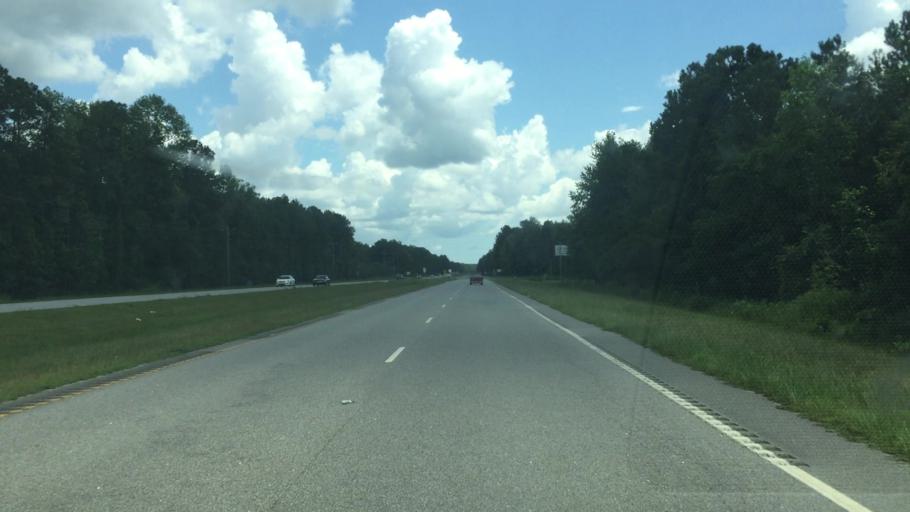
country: US
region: South Carolina
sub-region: Horry County
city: Loris
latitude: 34.0422
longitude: -78.8242
